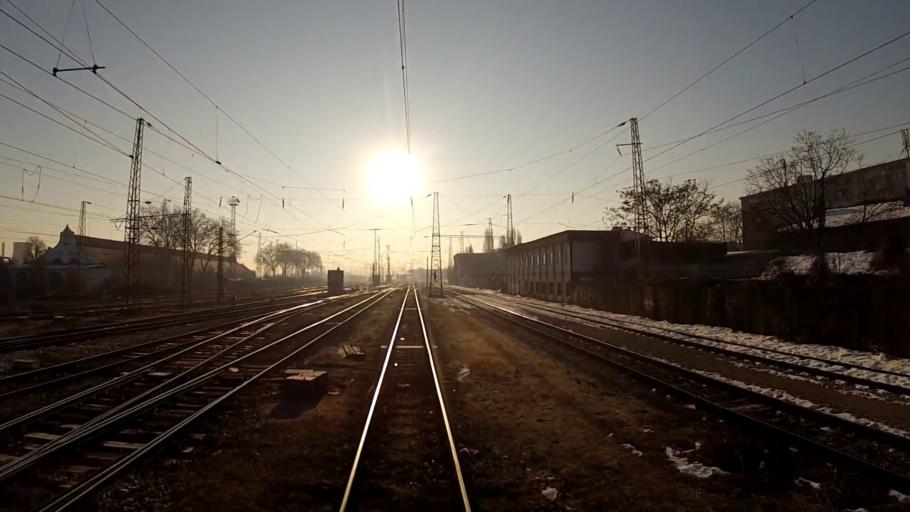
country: BG
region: Sofia-Capital
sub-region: Stolichna Obshtina
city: Sofia
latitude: 42.7227
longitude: 23.2952
